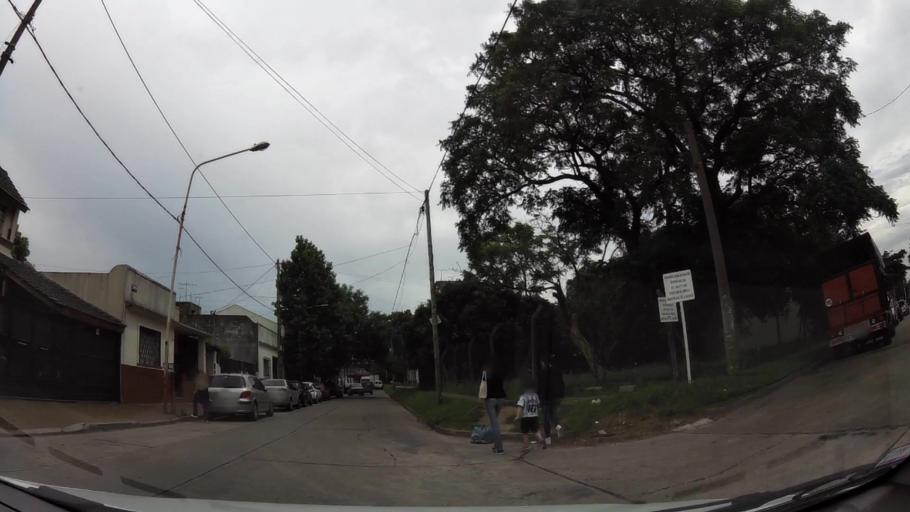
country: AR
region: Buenos Aires
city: San Justo
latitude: -34.6657
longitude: -58.5240
